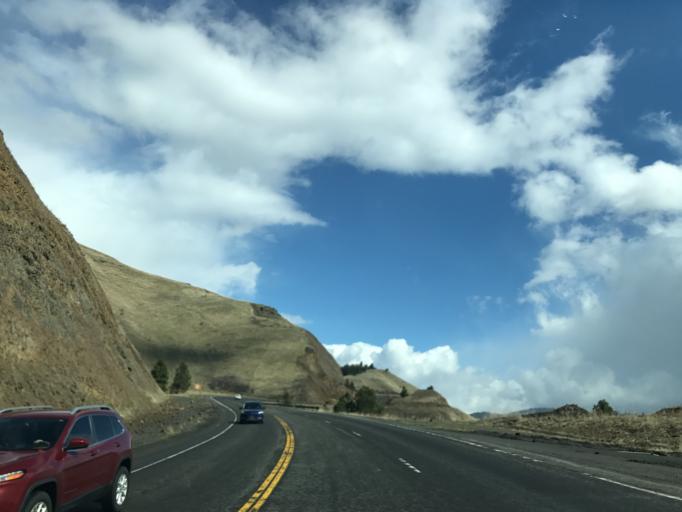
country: US
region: Idaho
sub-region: Idaho County
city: Grangeville
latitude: 45.8296
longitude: -116.2456
